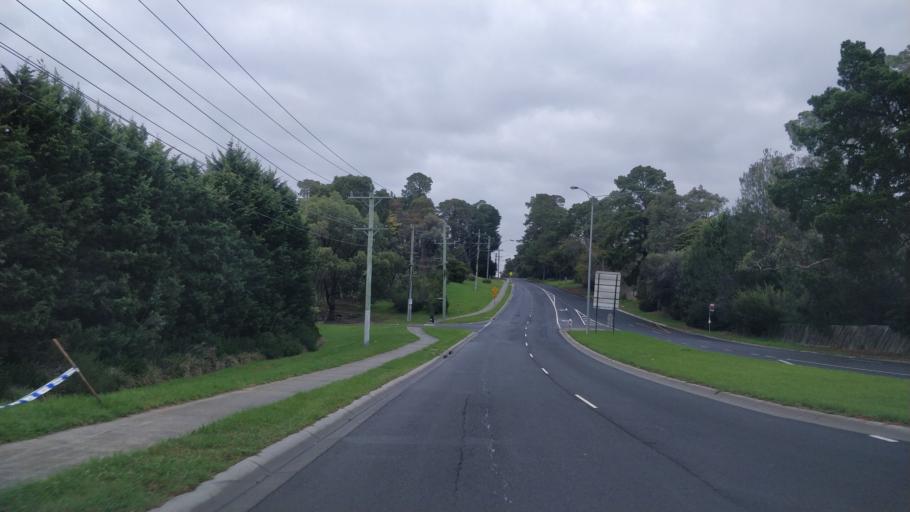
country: AU
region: Victoria
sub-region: Manningham
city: Donvale
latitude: -37.7847
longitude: 145.1815
